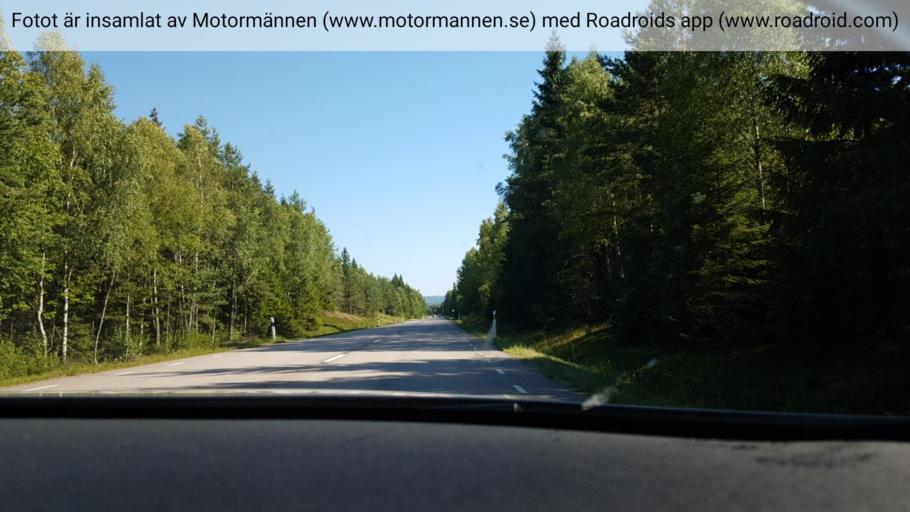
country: SE
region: Vaestra Goetaland
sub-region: Skara Kommun
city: Skara
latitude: 58.3036
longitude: 13.4675
